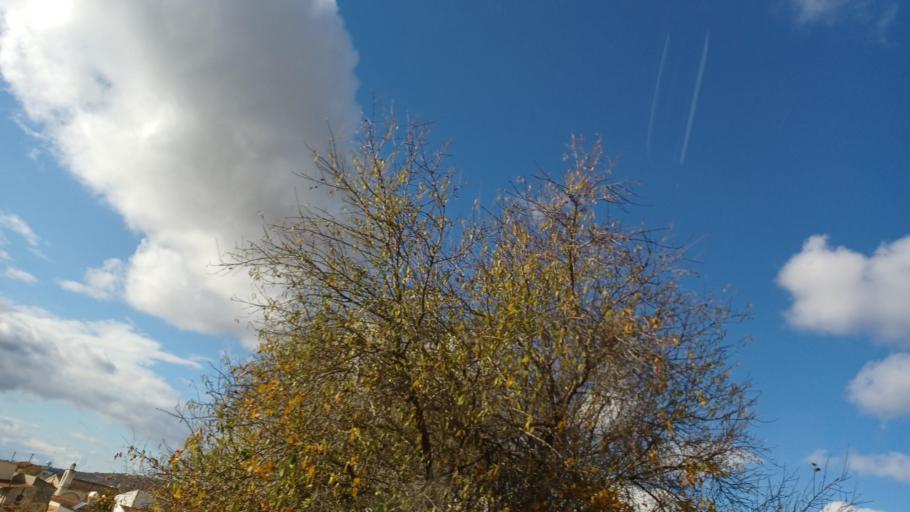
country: CY
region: Limassol
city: Pachna
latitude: 34.7815
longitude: 32.8279
